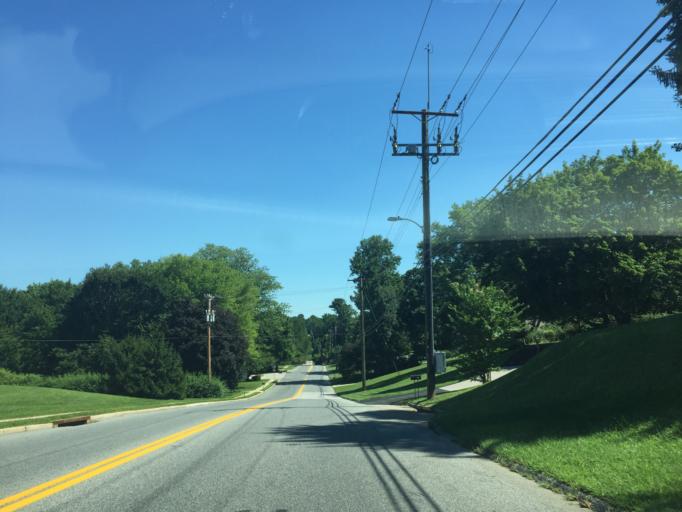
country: US
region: Maryland
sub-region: Baltimore County
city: Timonium
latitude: 39.4524
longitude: -76.6061
